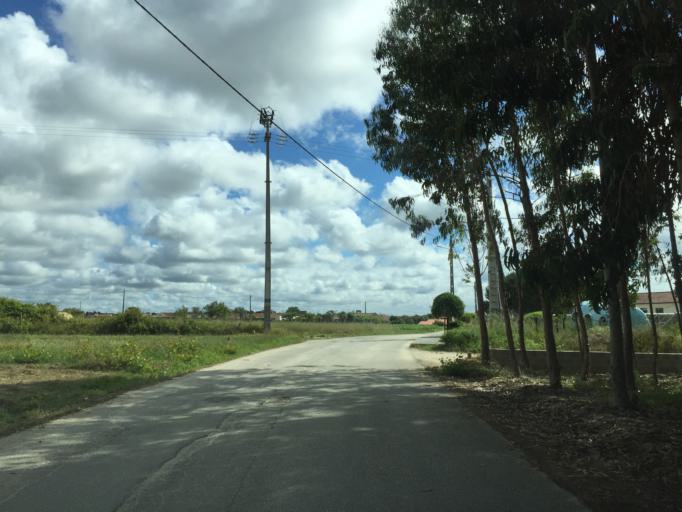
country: PT
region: Leiria
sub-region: Pombal
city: Lourical
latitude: 39.9867
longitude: -8.8040
